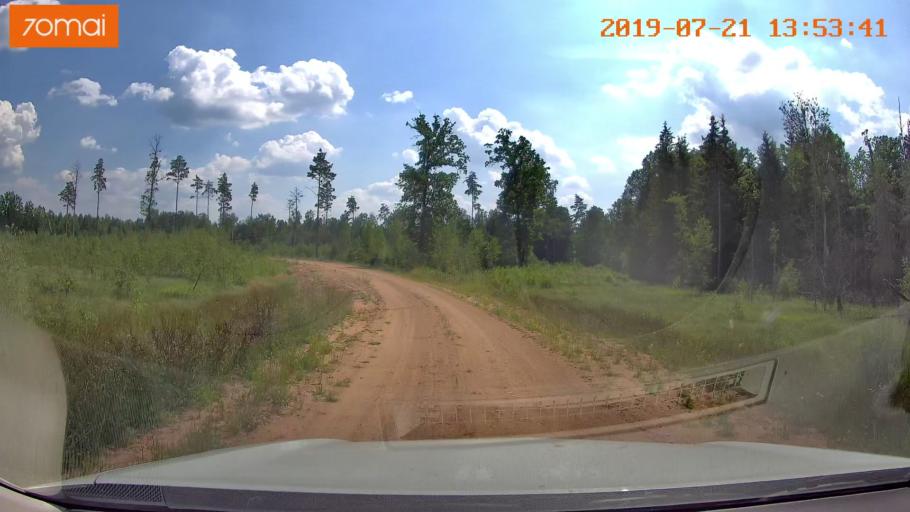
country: BY
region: Grodnenskaya
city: Lyubcha
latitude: 53.7774
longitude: 26.0650
